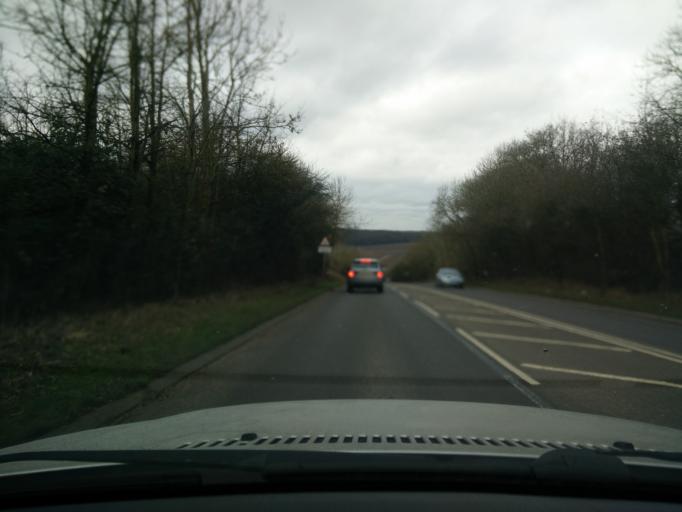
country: GB
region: England
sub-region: Buckinghamshire
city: Amersham
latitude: 51.6564
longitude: -0.6146
